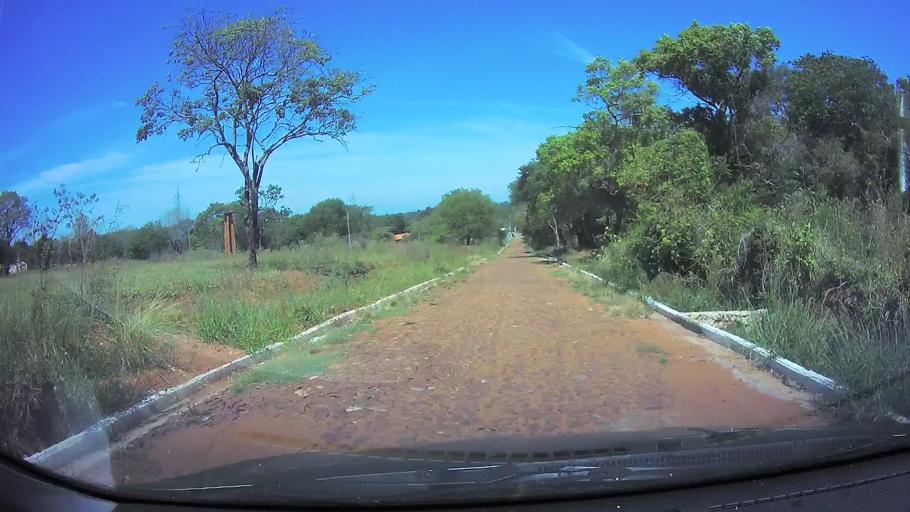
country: PY
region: Central
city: Limpio
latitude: -25.2300
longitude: -57.4367
